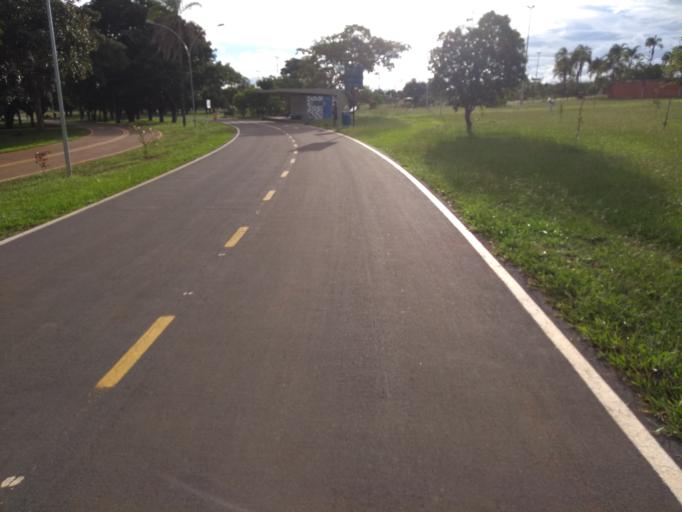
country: BR
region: Federal District
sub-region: Brasilia
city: Brasilia
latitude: -15.8092
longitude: -47.9193
